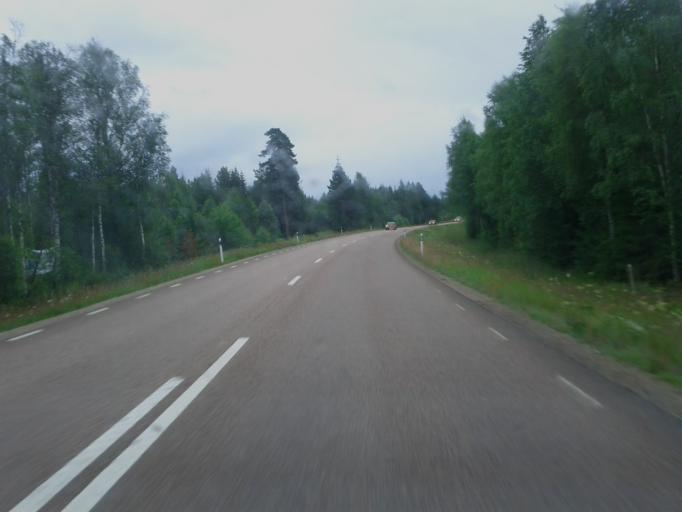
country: SE
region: Dalarna
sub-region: Mora Kommun
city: Mora
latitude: 60.9880
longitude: 14.6804
